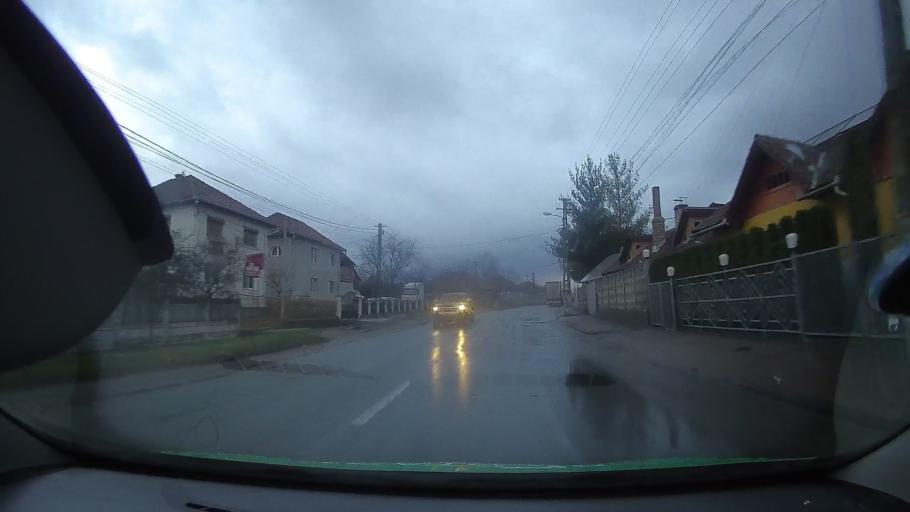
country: RO
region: Hunedoara
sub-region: Municipiul Brad
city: Brad
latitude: 46.1395
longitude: 22.7778
